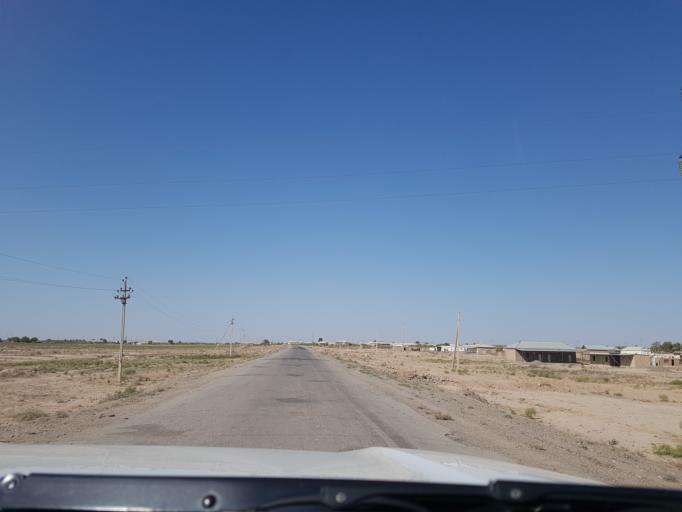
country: IR
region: Razavi Khorasan
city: Sarakhs
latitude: 36.5091
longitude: 61.2533
